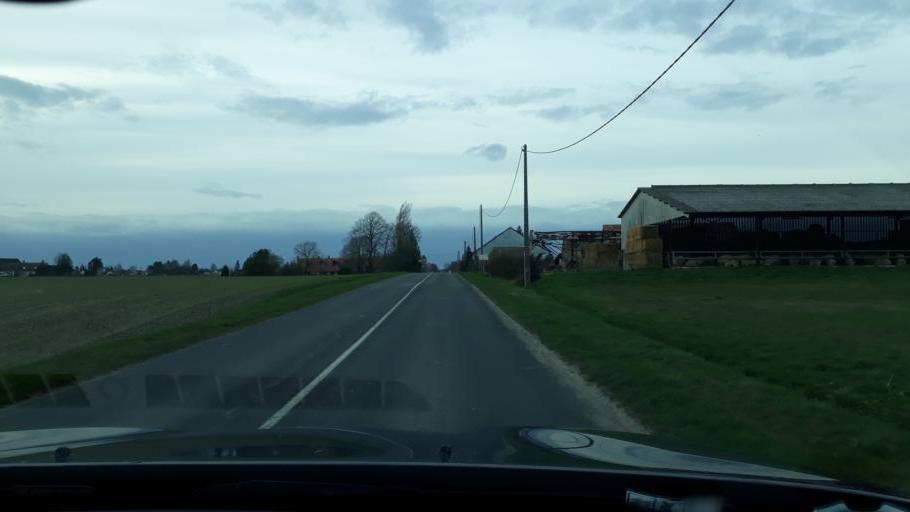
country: FR
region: Centre
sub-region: Departement du Loiret
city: Chilleurs-aux-Bois
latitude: 48.0662
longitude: 2.1476
